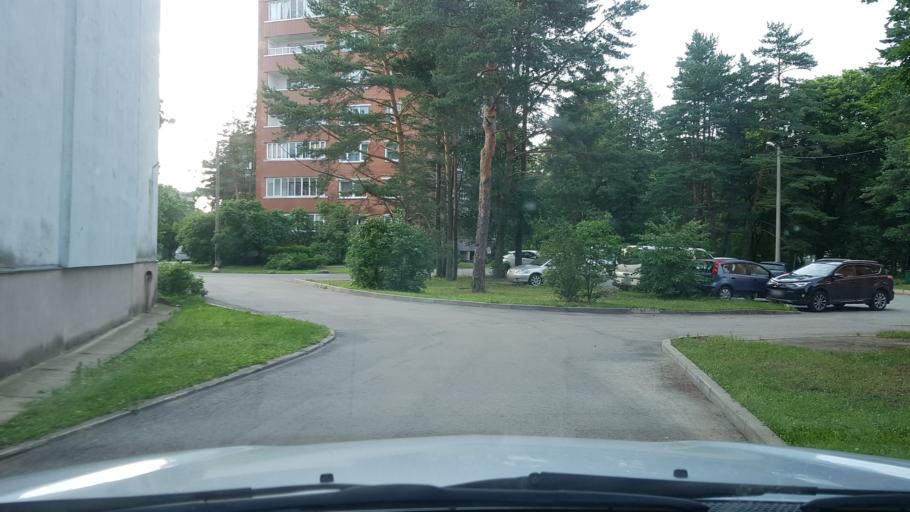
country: EE
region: Ida-Virumaa
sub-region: Narva-Joesuu linn
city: Narva-Joesuu
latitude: 59.4592
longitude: 28.0488
